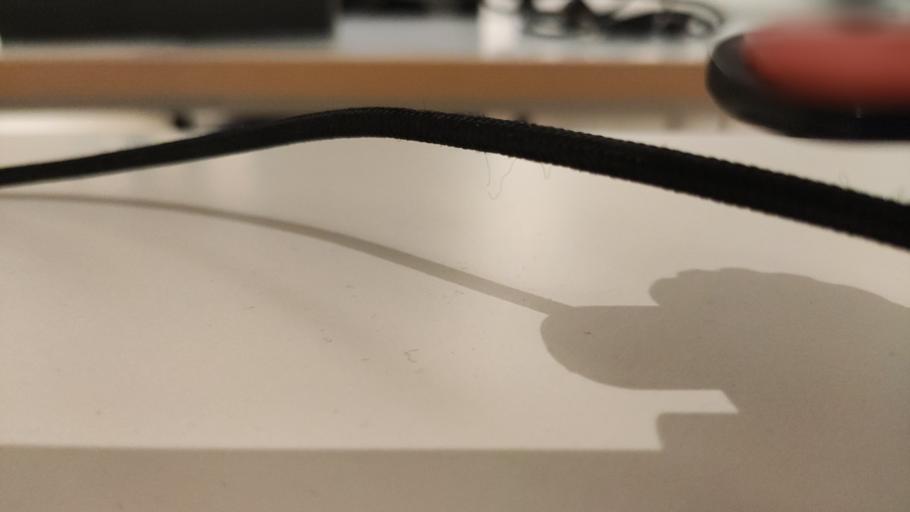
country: RU
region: Moskovskaya
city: Dorokhovo
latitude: 55.4560
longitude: 36.3532
